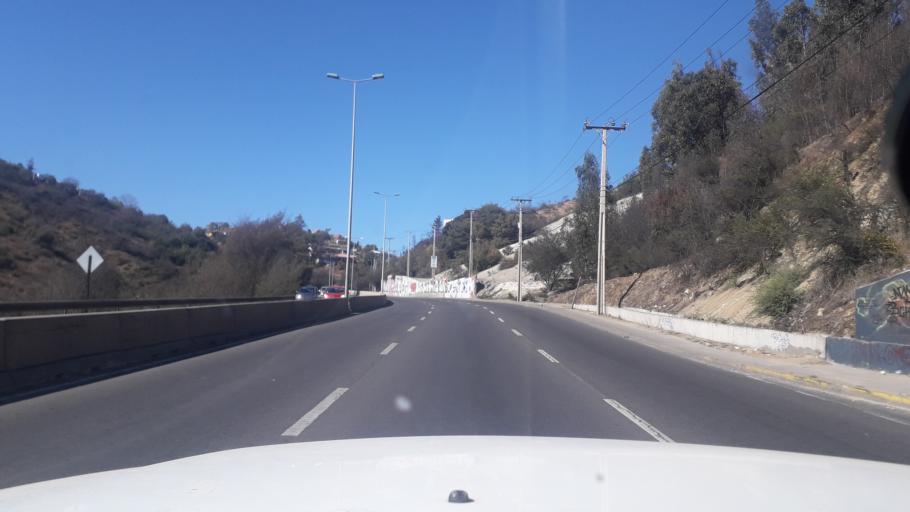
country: CL
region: Valparaiso
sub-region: Provincia de Valparaiso
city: Vina del Mar
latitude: -33.0351
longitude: -71.5141
